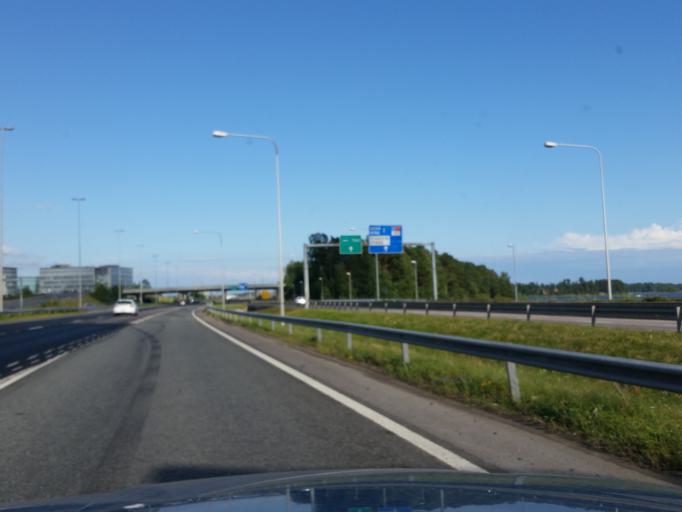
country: FI
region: Uusimaa
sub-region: Helsinki
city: Otaniemi
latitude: 60.1695
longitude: 24.8175
